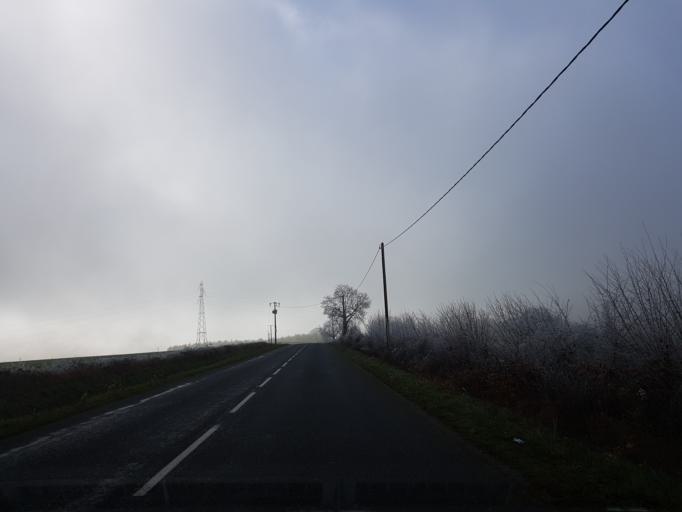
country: FR
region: Bourgogne
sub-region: Departement de Saone-et-Loire
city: Saint-Berain-sous-Sanvignes
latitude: 46.7258
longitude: 4.2813
